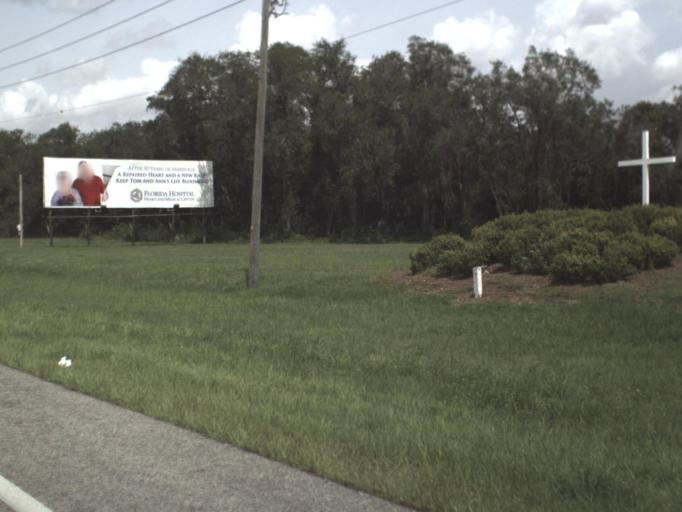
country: US
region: Florida
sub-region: Highlands County
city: Avon Park
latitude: 27.5399
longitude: -81.5041
